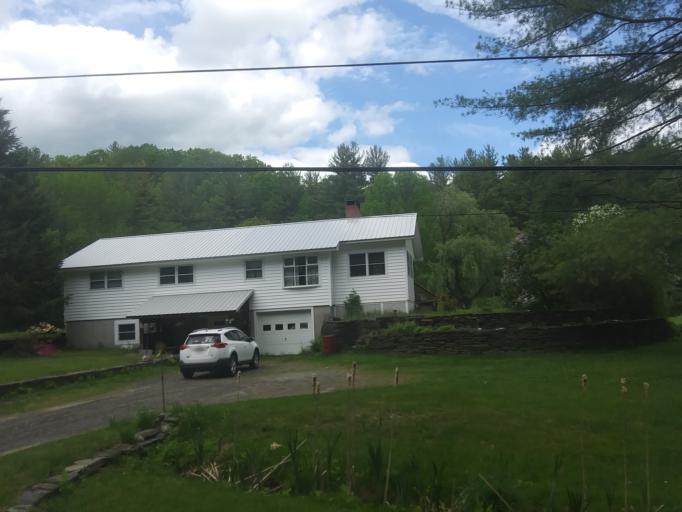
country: US
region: Massachusetts
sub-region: Franklin County
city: Buckland
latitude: 42.5842
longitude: -72.8341
